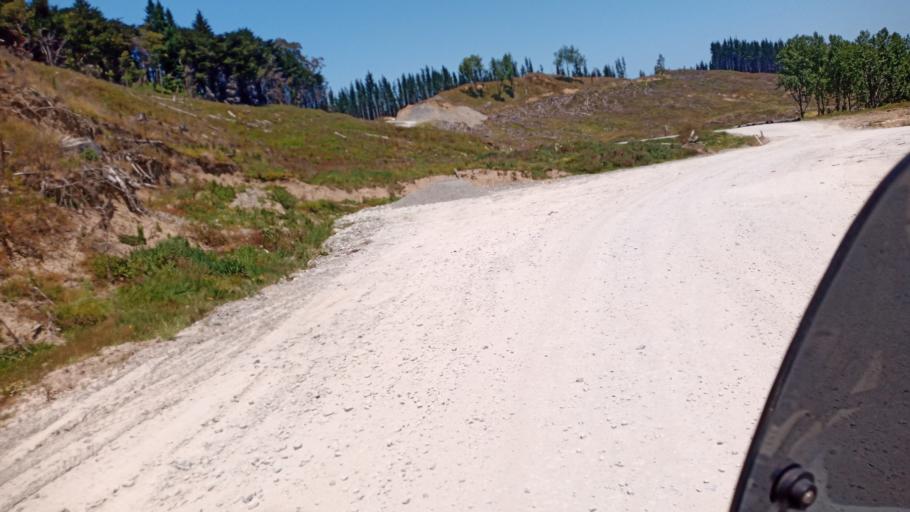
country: NZ
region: Gisborne
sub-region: Gisborne District
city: Gisborne
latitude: -38.2913
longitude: 178.0074
